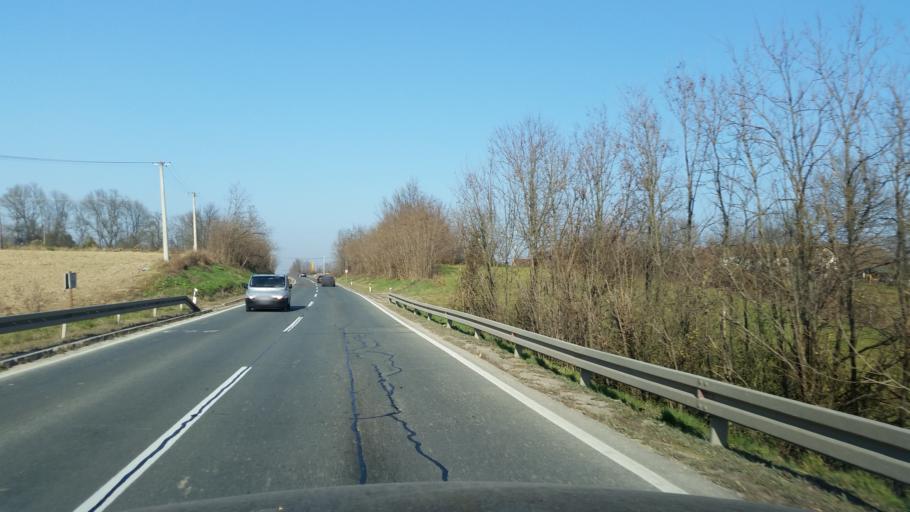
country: RS
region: Central Serbia
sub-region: Kolubarski Okrug
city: Ljig
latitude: 44.2576
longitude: 20.2865
